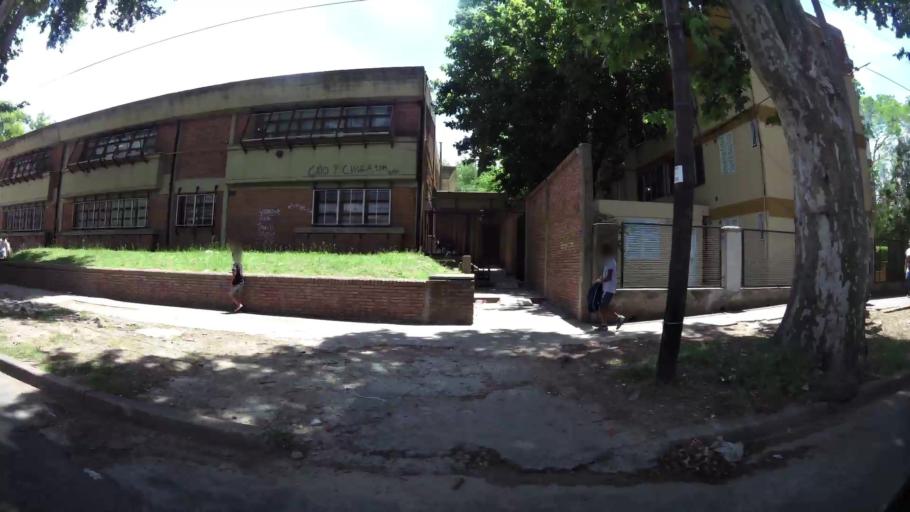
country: AR
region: Santa Fe
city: Gobernador Galvez
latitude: -32.9965
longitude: -60.6263
